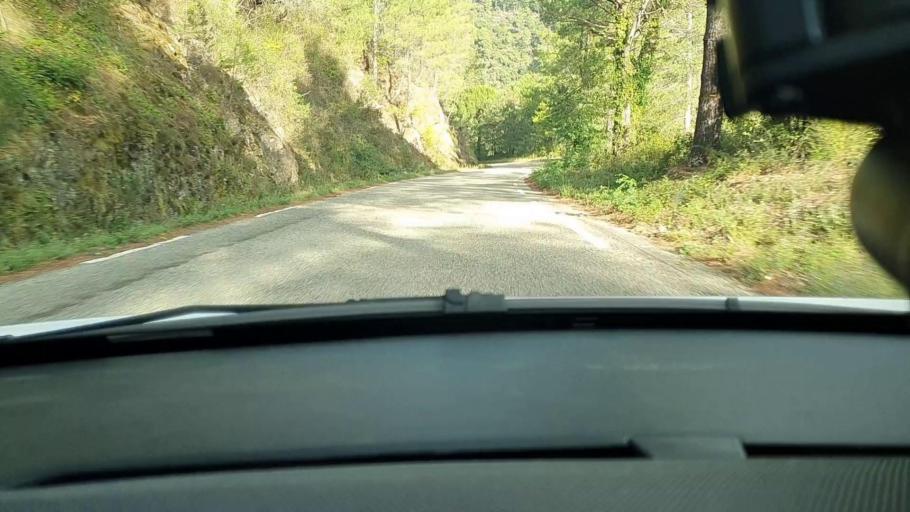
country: FR
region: Languedoc-Roussillon
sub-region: Departement du Gard
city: Besseges
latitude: 44.3158
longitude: 4.0430
